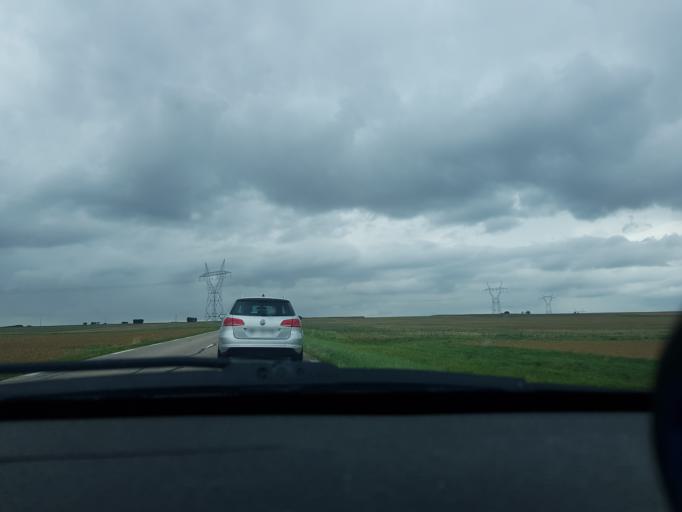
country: FR
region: Lorraine
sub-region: Departement de la Moselle
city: Faulquemont
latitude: 48.9908
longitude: 6.6000
